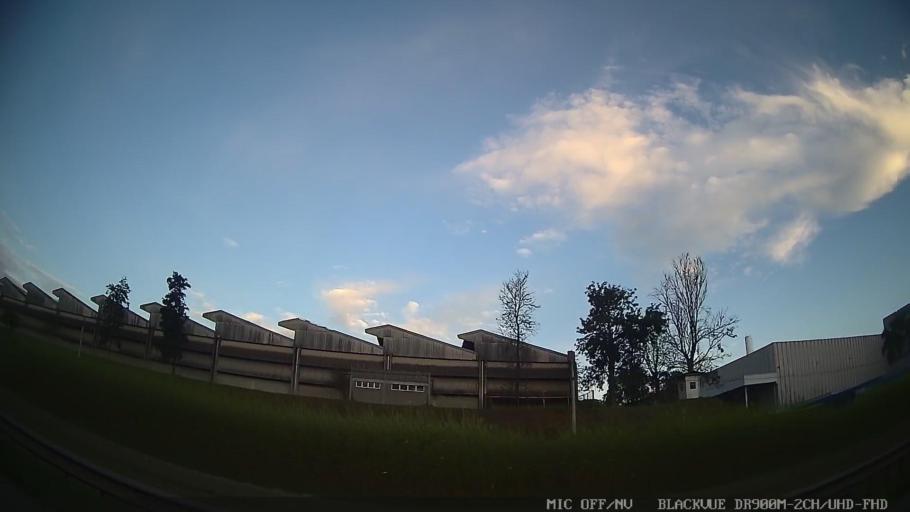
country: BR
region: Sao Paulo
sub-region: Indaiatuba
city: Indaiatuba
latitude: -23.1339
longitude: -47.2378
